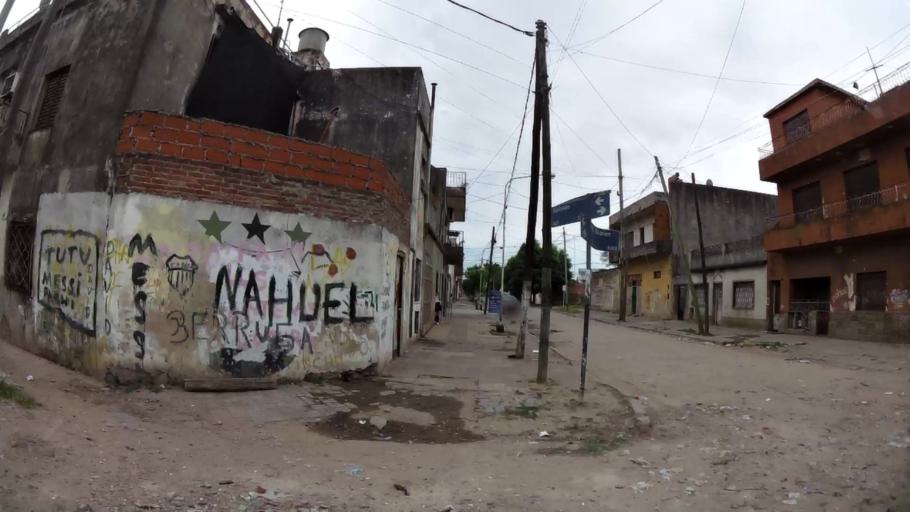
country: AR
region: Buenos Aires
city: San Justo
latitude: -34.6741
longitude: -58.5220
